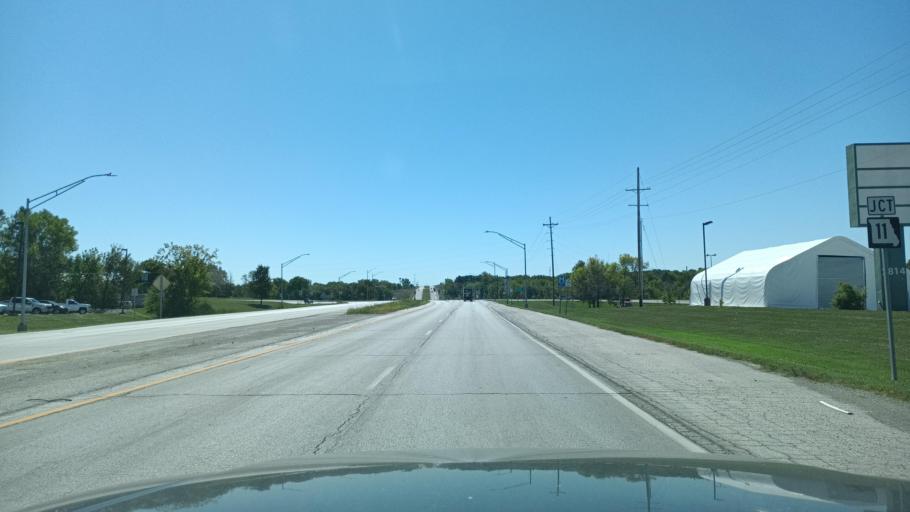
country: US
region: Missouri
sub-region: Adair County
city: Kirksville
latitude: 40.1707
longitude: -92.5721
